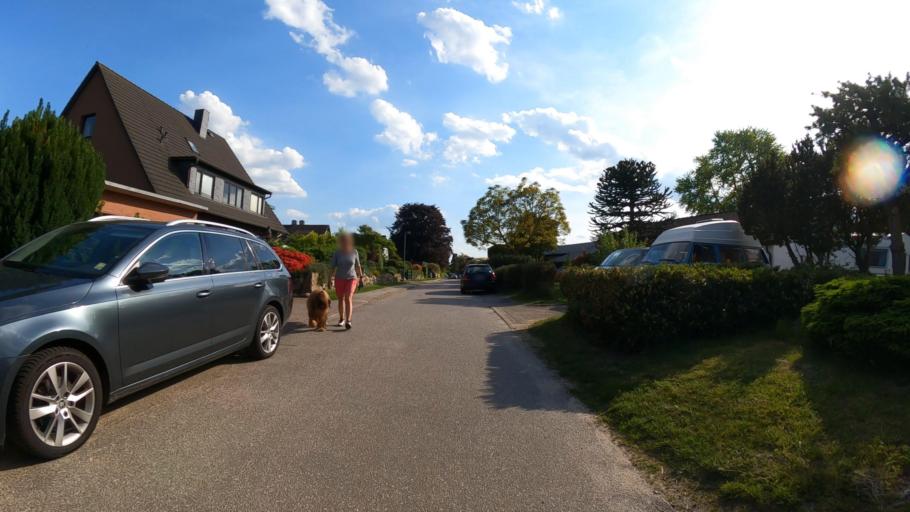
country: DE
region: Lower Saxony
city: Seevetal
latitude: 53.4088
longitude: 9.9665
